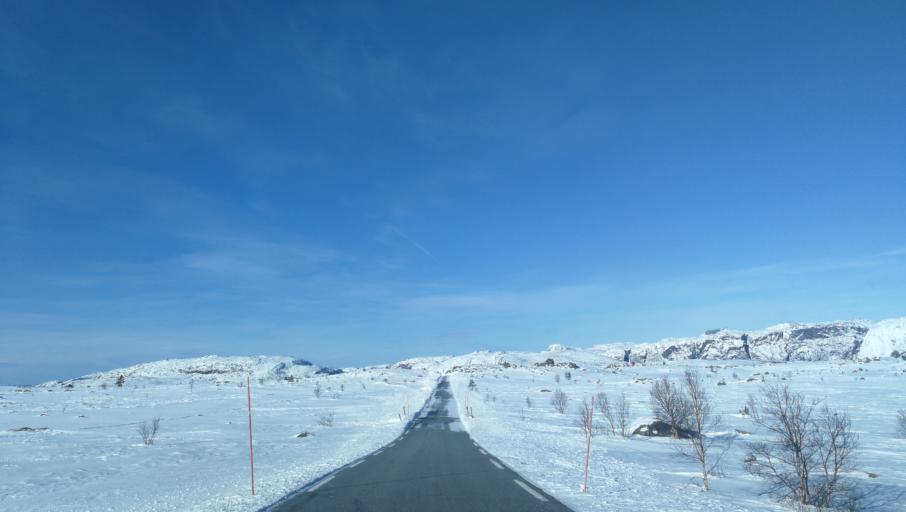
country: NO
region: Rogaland
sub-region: Hjelmeland
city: Hjelmelandsvagen
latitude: 59.1061
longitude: 6.3755
